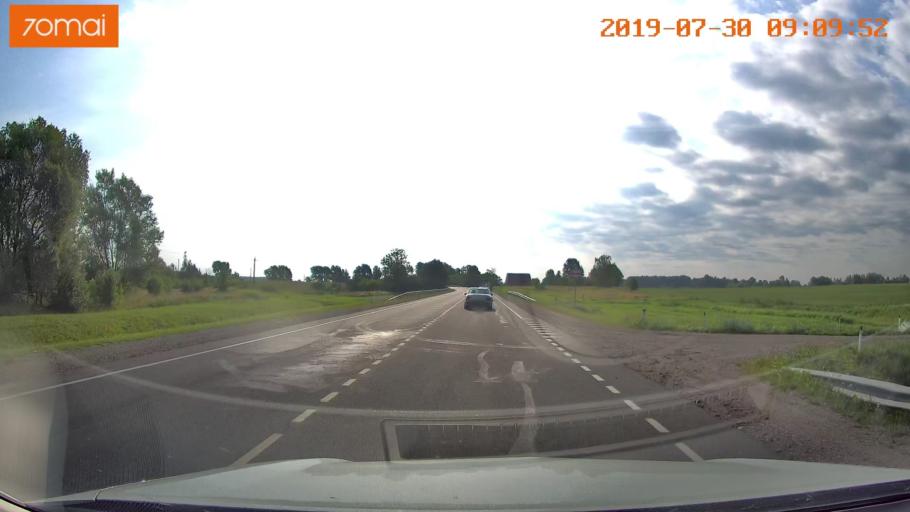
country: RU
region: Kaliningrad
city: Nesterov
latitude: 54.6124
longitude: 22.4165
